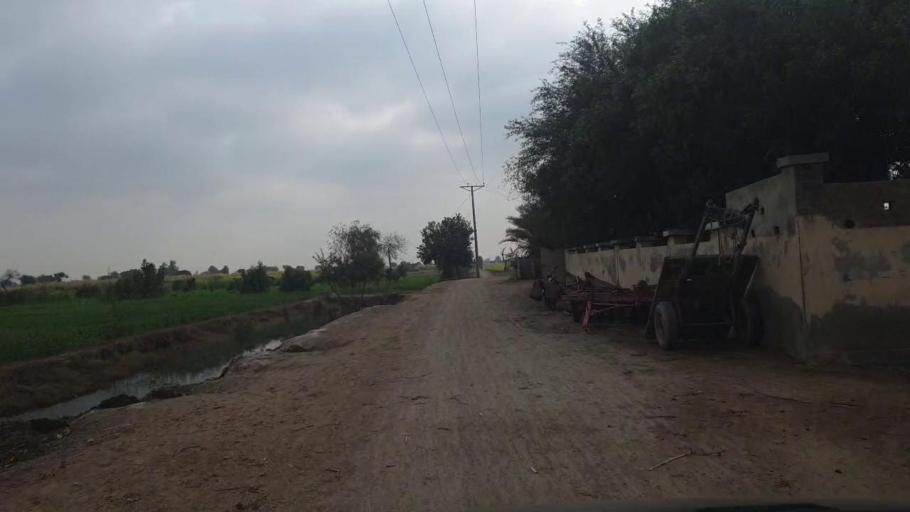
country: PK
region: Sindh
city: Shahdadpur
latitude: 25.8884
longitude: 68.7048
